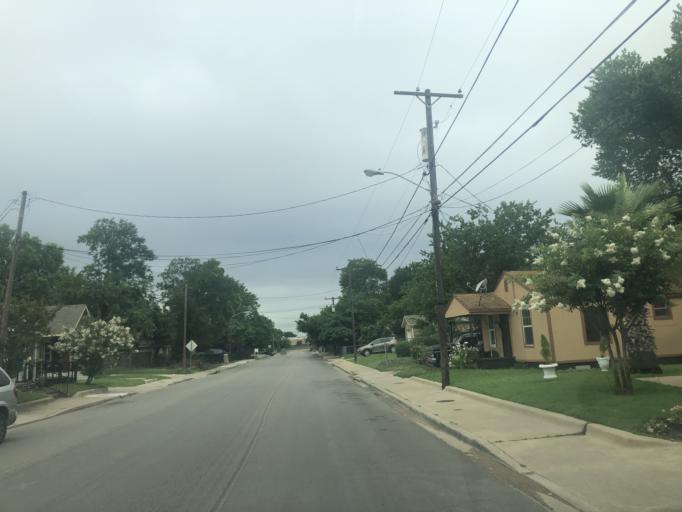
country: US
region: Texas
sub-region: Dallas County
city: Dallas
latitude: 32.7818
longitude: -96.8520
